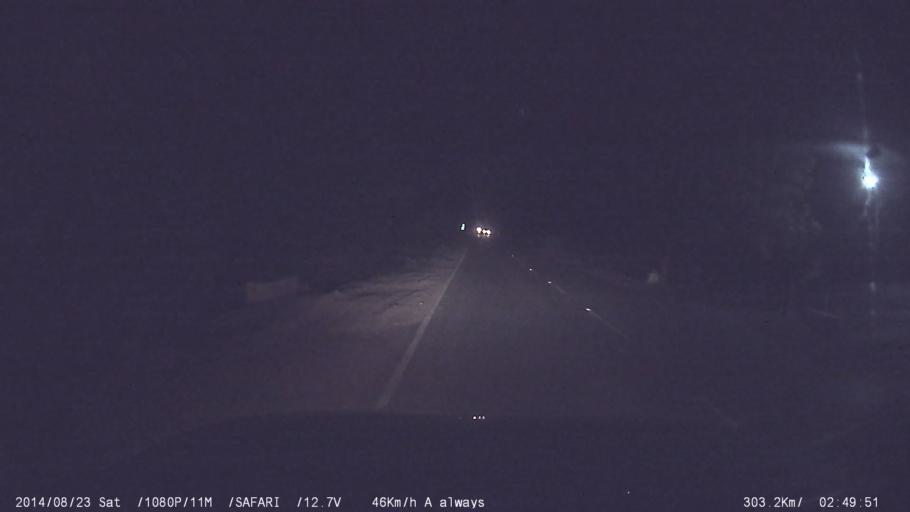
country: IN
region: Tamil Nadu
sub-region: Kancheepuram
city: Vandalur
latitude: 12.9227
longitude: 80.0177
